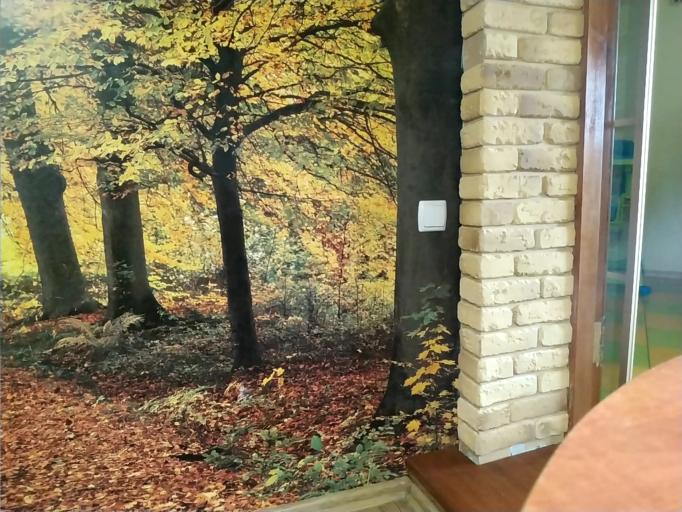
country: RU
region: Smolensk
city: Dorogobuzh
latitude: 54.8558
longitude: 33.3177
